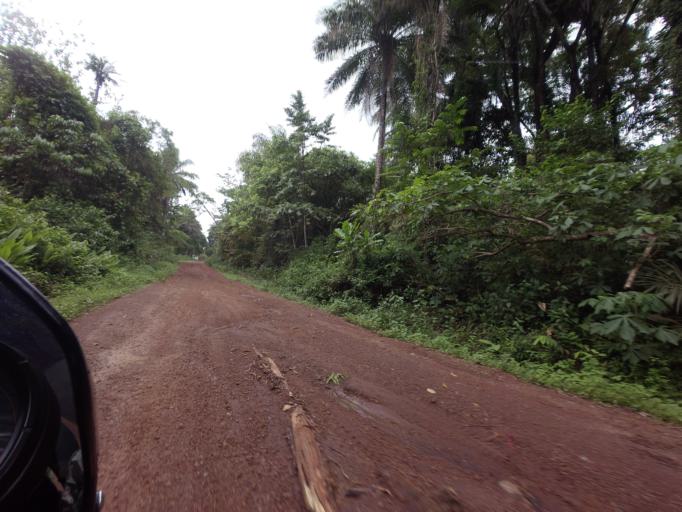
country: SL
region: Northern Province
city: Kambia
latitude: 9.0871
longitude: -13.0164
